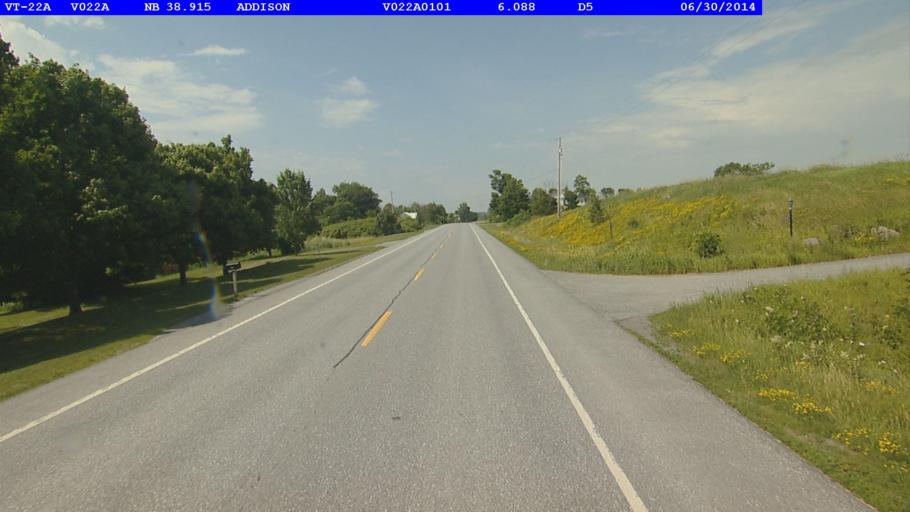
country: US
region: Vermont
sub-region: Addison County
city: Vergennes
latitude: 44.1163
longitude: -73.2936
